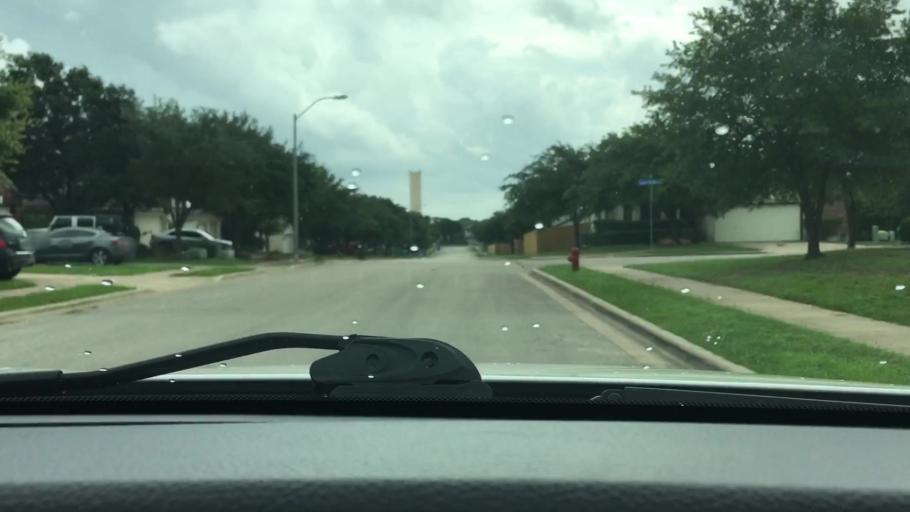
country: US
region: Texas
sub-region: Travis County
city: Windemere
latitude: 30.4750
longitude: -97.6513
